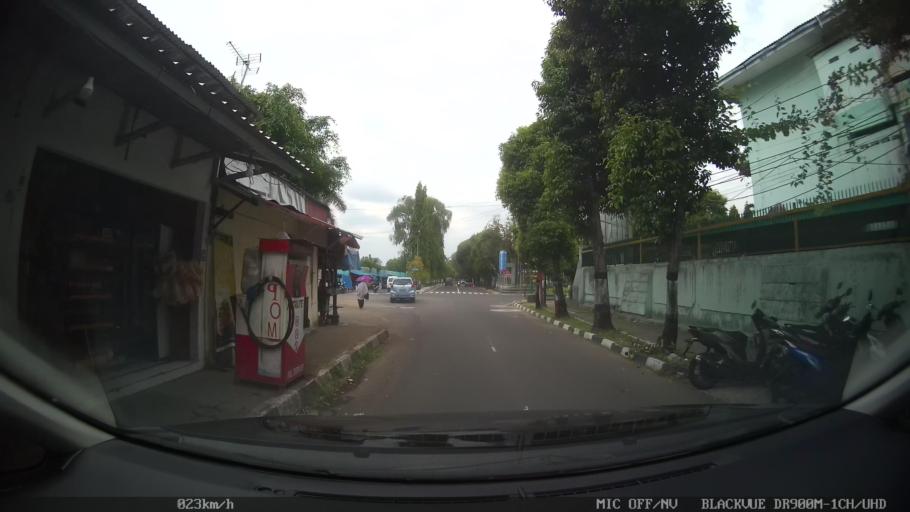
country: ID
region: Daerah Istimewa Yogyakarta
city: Yogyakarta
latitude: -7.7941
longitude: 110.3835
